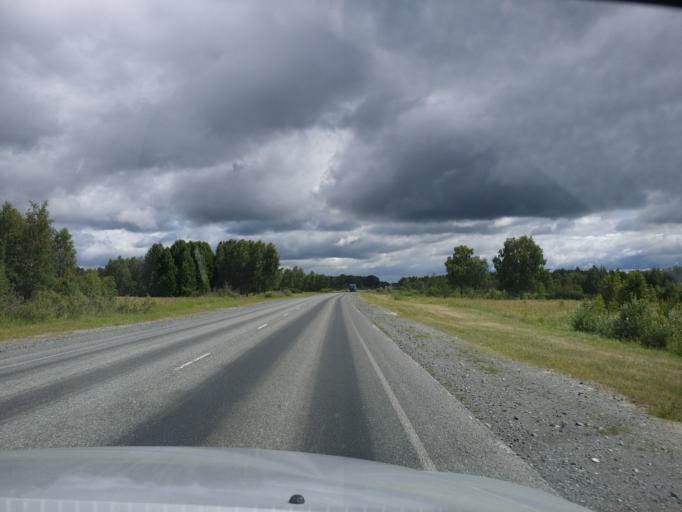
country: RU
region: Tjumen
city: Yarkovo
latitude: 57.5920
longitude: 67.2433
